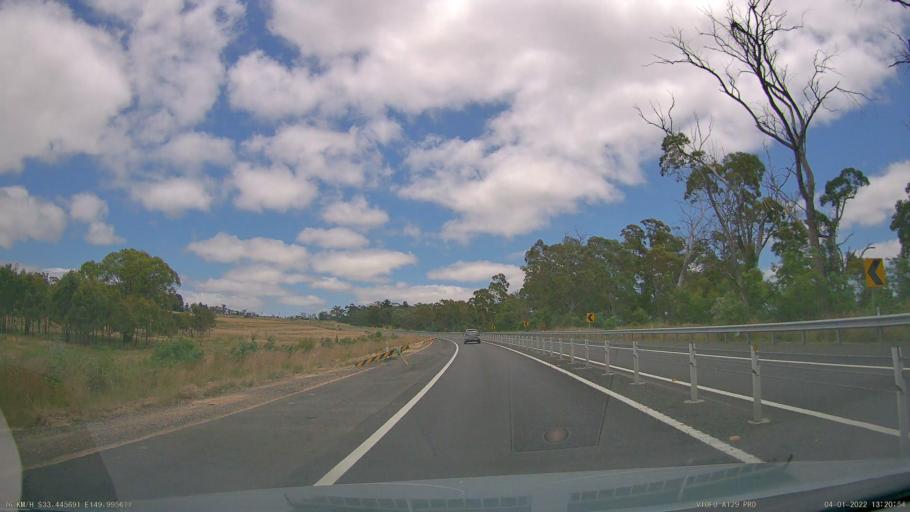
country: AU
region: New South Wales
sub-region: Lithgow
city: Portland
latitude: -33.4458
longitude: 149.9952
